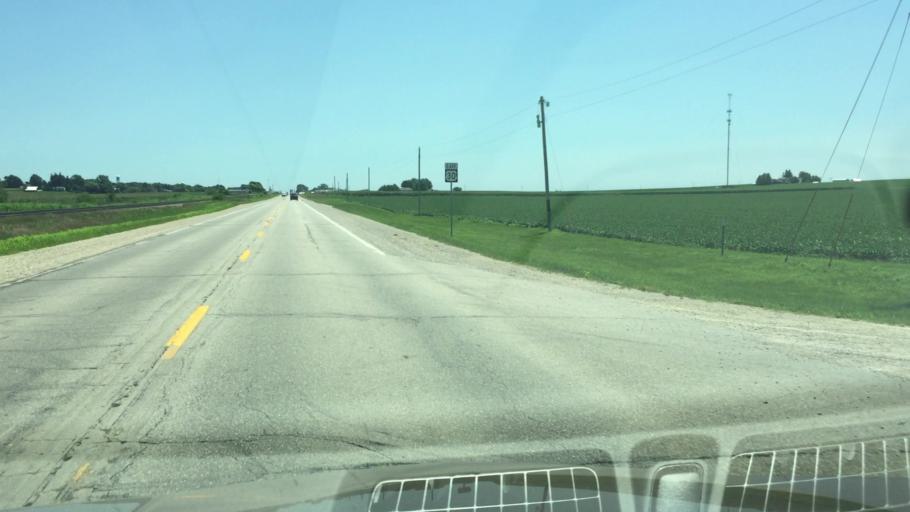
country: US
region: Iowa
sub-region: Cedar County
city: Mechanicsville
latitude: 41.9083
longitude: -91.2786
